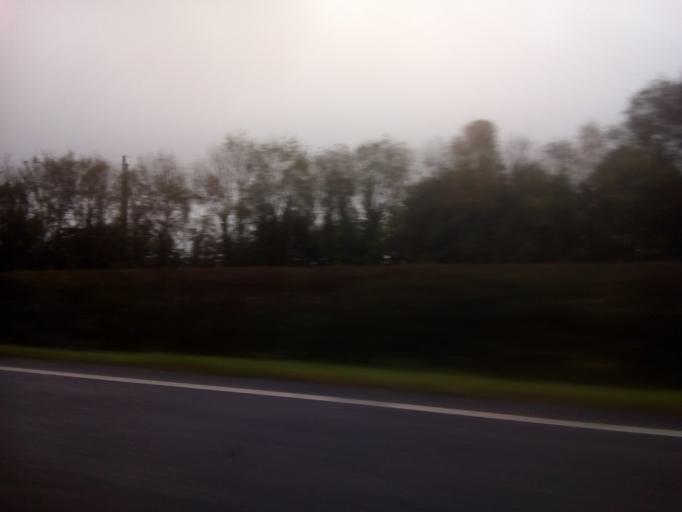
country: IE
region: Leinster
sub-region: An Iarmhi
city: An Muileann gCearr
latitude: 53.5381
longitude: -7.3127
